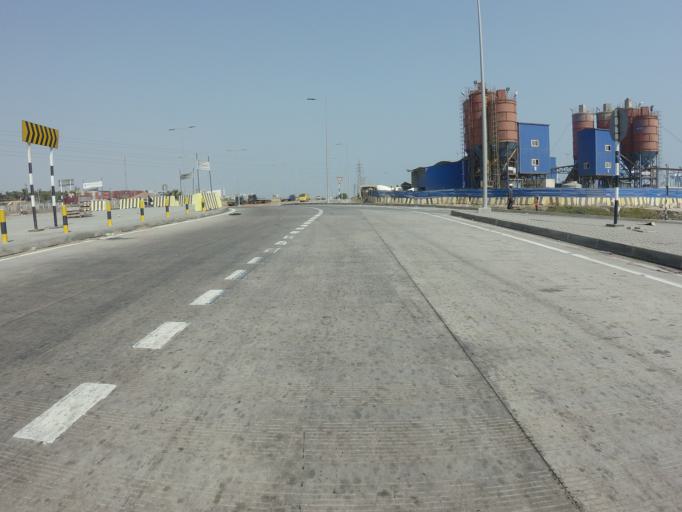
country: GH
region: Greater Accra
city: Tema
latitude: 5.6168
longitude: -0.0228
